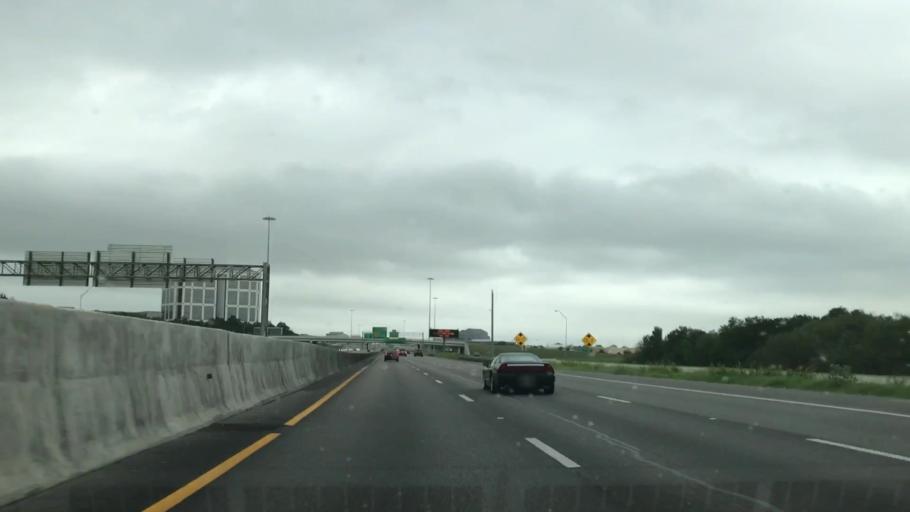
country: US
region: Texas
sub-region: Dallas County
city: Farmers Branch
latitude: 32.8844
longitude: -96.9516
